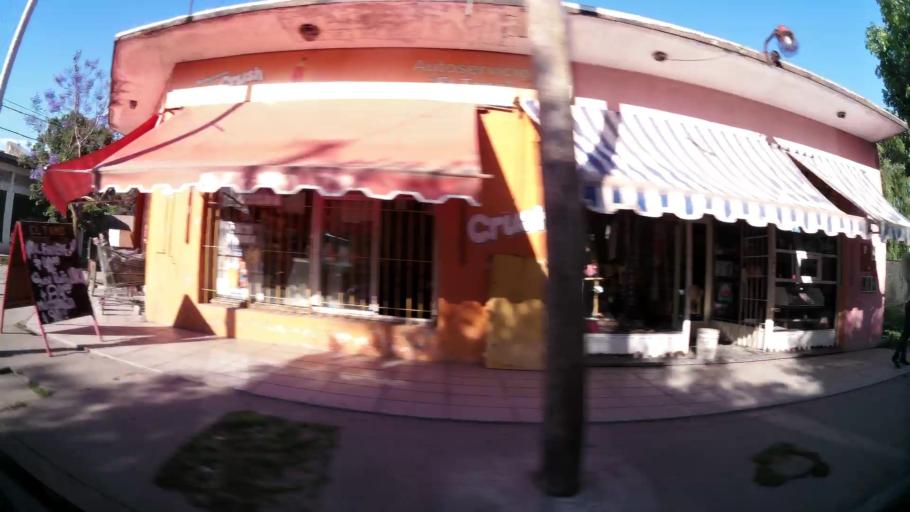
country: AR
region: Buenos Aires
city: Santa Catalina - Dique Lujan
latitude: -34.4955
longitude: -58.7194
